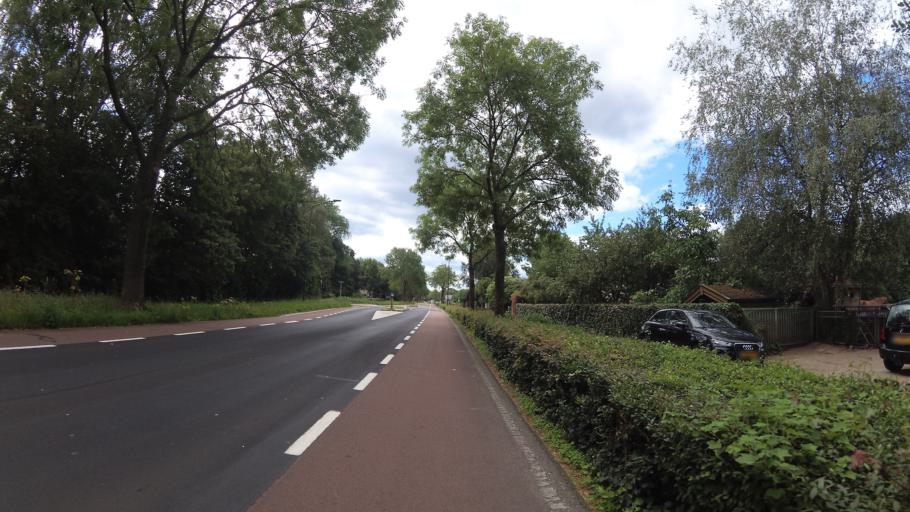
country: NL
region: North Brabant
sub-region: Gemeente Dongen
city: Dongen
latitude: 51.6332
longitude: 4.9195
